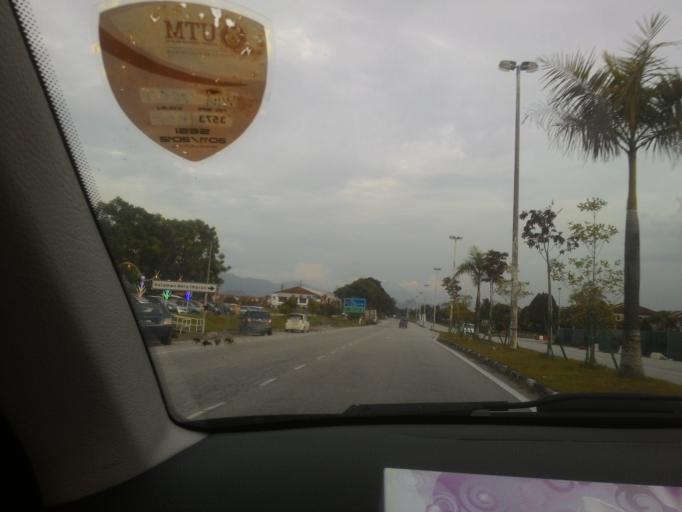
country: MY
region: Perak
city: Ipoh
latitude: 4.6751
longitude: 101.0826
